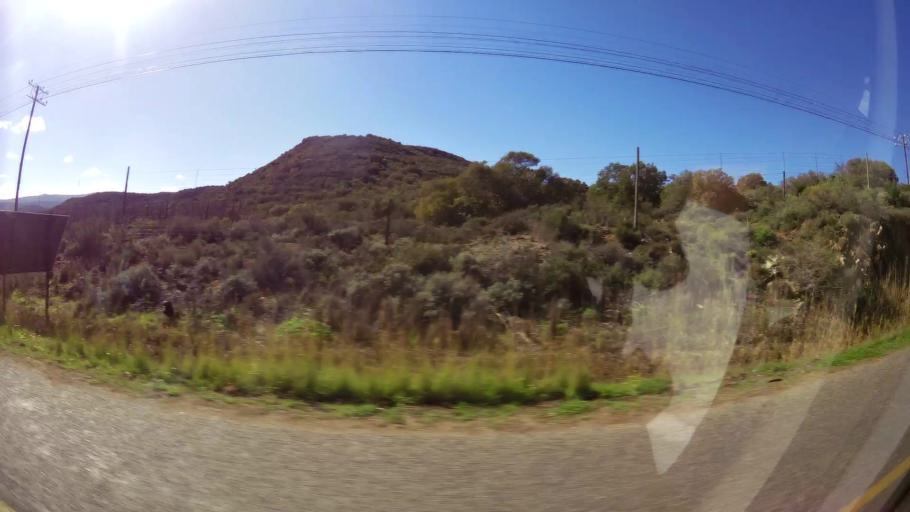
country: ZA
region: Western Cape
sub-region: Cape Winelands District Municipality
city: Ashton
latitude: -33.7910
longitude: 20.1369
